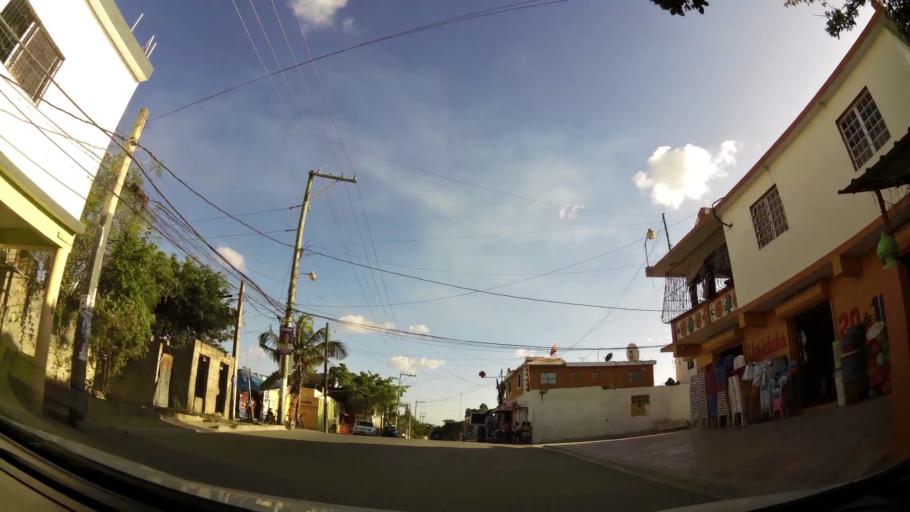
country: DO
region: Santo Domingo
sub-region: Santo Domingo
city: Santo Domingo Este
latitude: 18.4740
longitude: -69.7945
